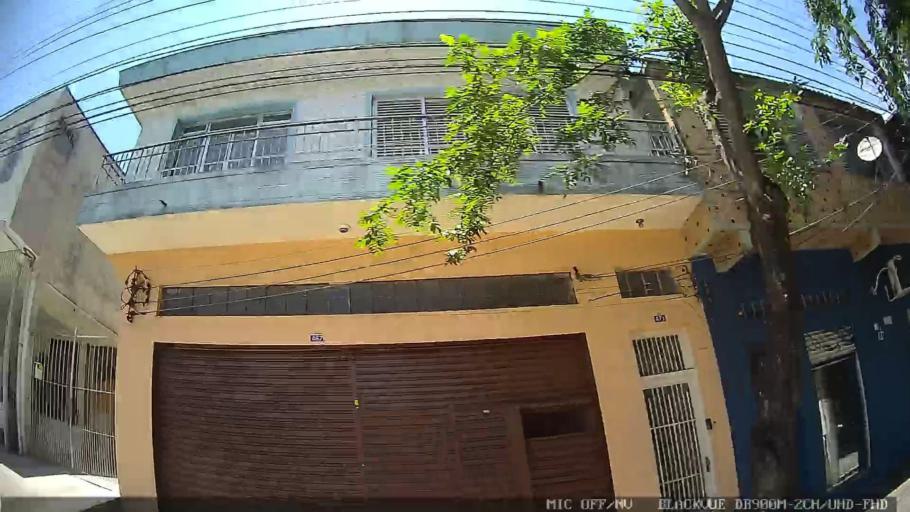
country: BR
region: Sao Paulo
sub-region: Sao Caetano Do Sul
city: Sao Caetano do Sul
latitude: -23.5592
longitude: -46.5664
